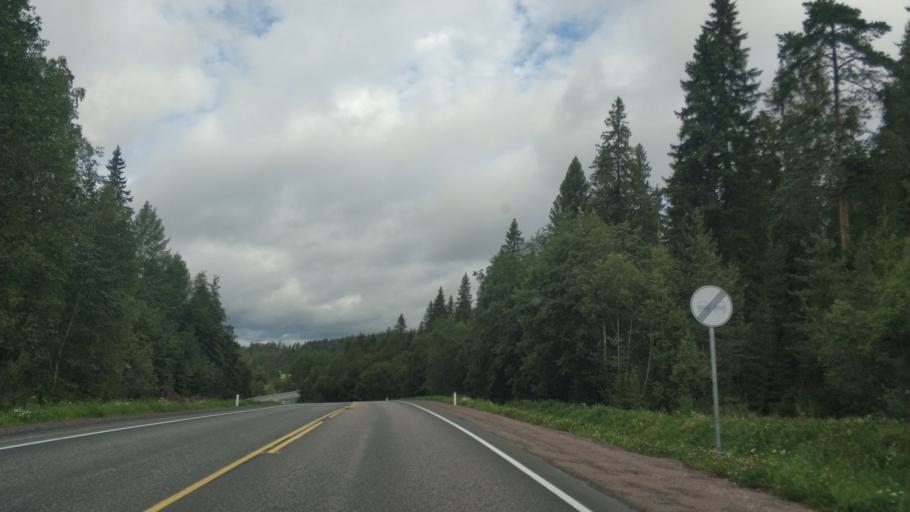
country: RU
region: Republic of Karelia
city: Khelyulya
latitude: 61.7950
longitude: 30.6226
